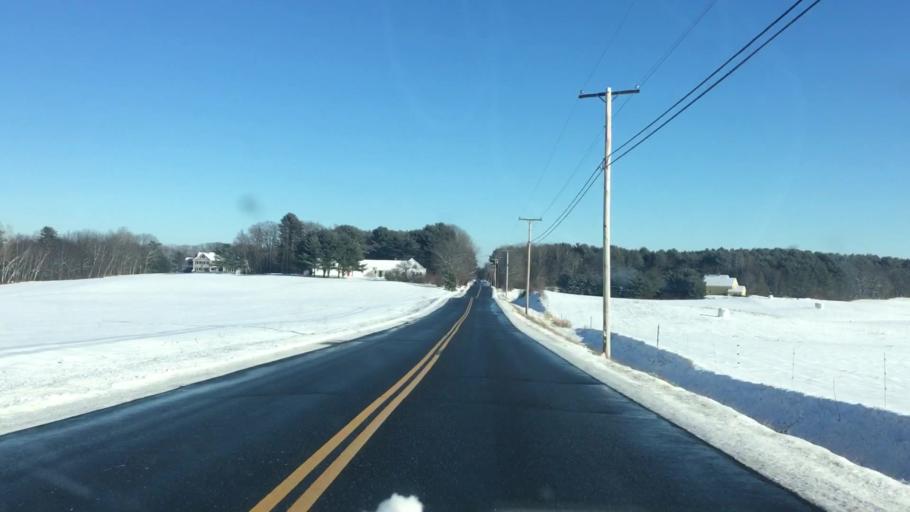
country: US
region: Maine
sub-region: Androscoggin County
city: Lisbon Falls
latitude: 43.9491
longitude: -70.1070
